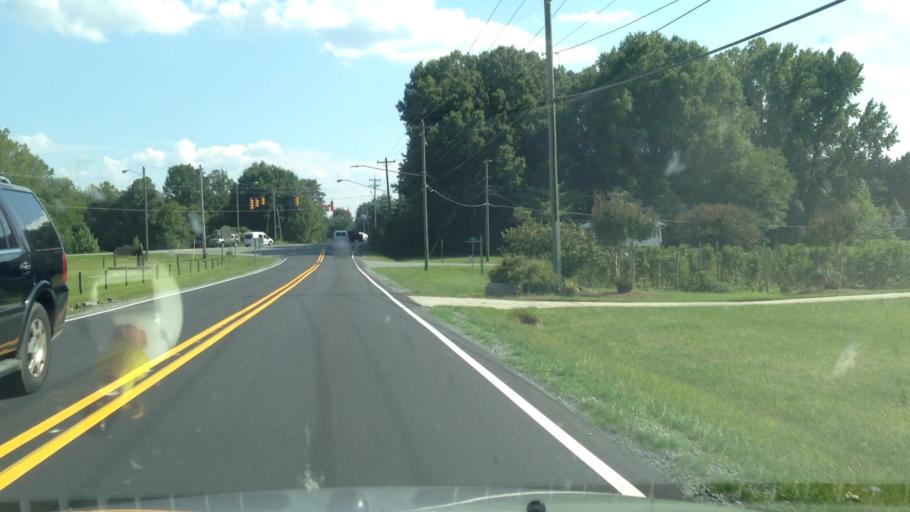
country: US
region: North Carolina
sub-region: Forsyth County
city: Walkertown
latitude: 36.1574
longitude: -80.1461
